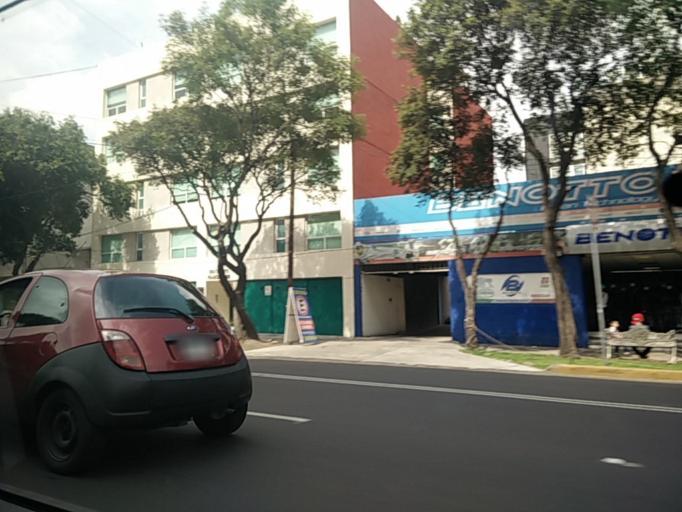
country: MX
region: Mexico City
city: Colonia del Valle
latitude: 19.3731
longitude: -99.1607
